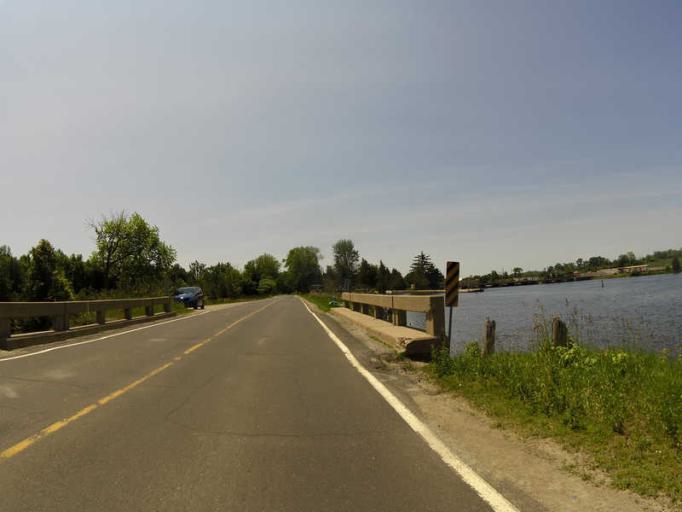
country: CA
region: Ontario
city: Peterborough
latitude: 44.4023
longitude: -78.2619
